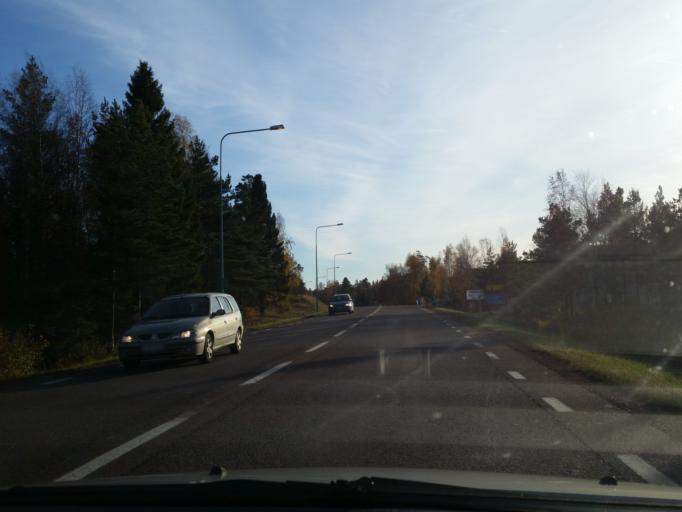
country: AX
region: Mariehamns stad
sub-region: Mariehamn
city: Mariehamn
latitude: 60.1254
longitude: 19.9338
